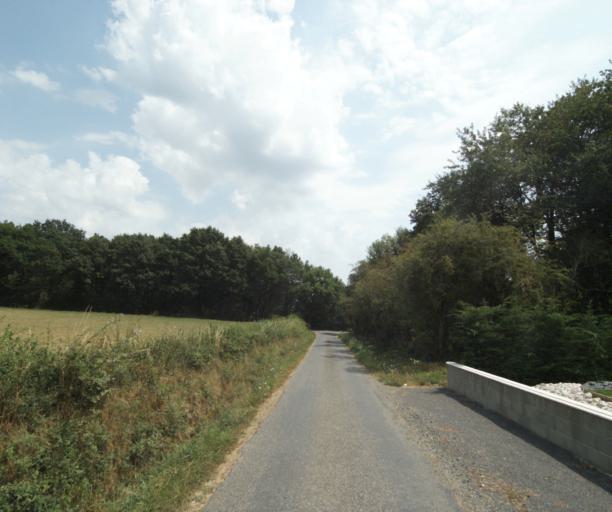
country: FR
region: Bourgogne
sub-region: Departement de Saone-et-Loire
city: Gueugnon
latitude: 46.5884
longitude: 4.0295
